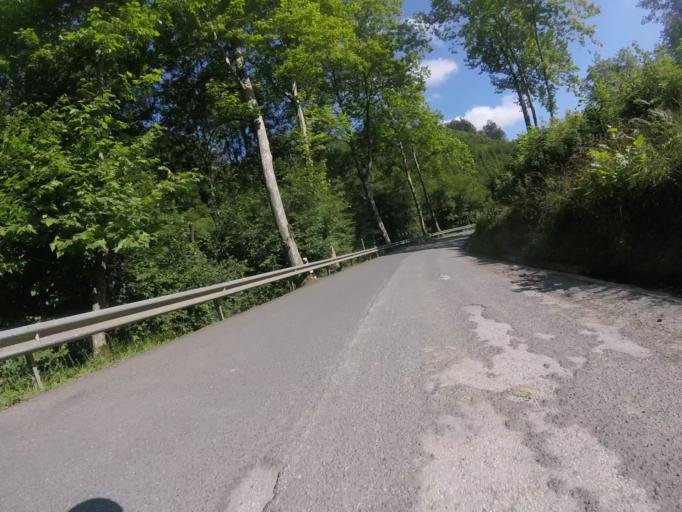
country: ES
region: Basque Country
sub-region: Provincia de Guipuzcoa
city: Ormaiztegui
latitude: 43.0968
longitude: -2.2486
